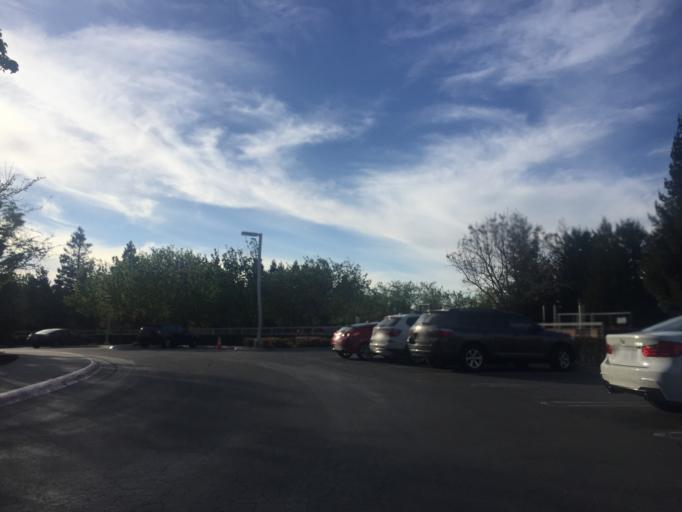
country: US
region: California
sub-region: Santa Clara County
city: Mountain View
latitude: 37.4232
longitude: -122.0886
